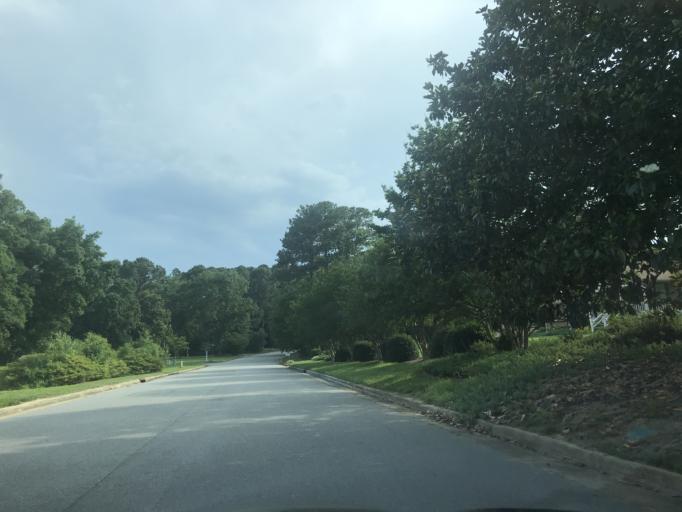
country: US
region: North Carolina
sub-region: Wake County
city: Knightdale
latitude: 35.8235
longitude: -78.5455
